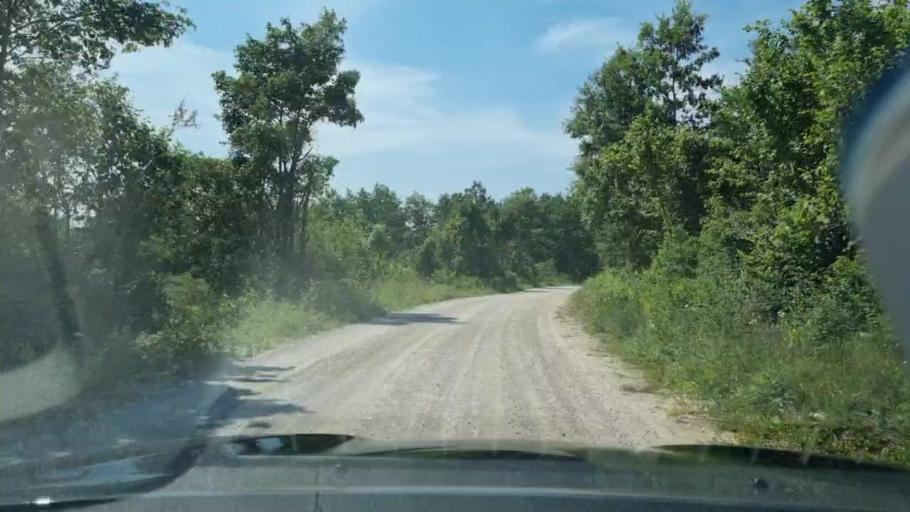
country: BA
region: Federation of Bosnia and Herzegovina
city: Orasac
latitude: 44.6292
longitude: 16.2863
